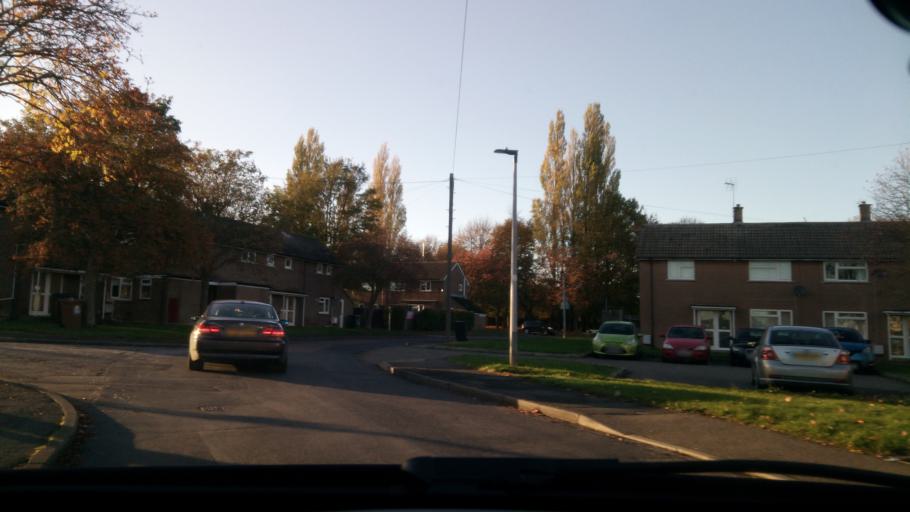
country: GB
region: England
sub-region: Peterborough
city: Wittering
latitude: 52.6092
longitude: -0.4384
